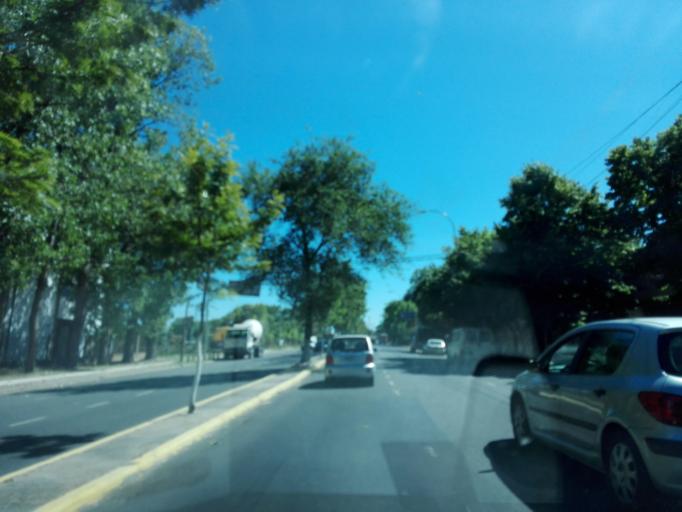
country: AR
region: Buenos Aires
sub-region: Partido de La Plata
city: La Plata
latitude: -34.9045
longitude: -57.9244
